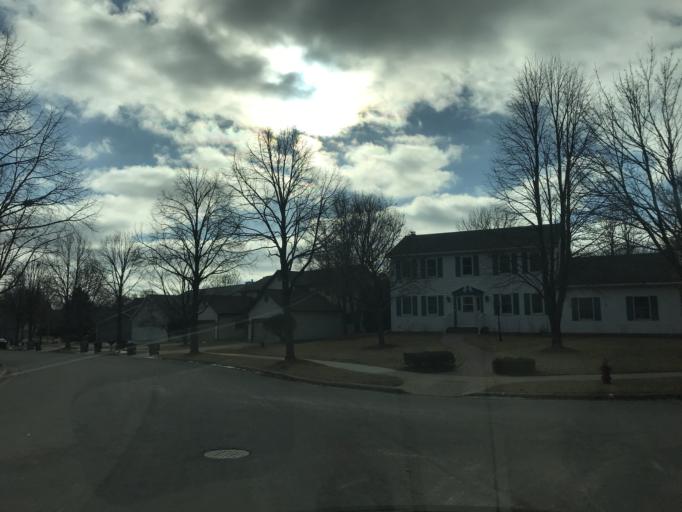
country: US
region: Wisconsin
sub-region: Dane County
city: Monona
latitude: 43.1155
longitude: -89.2981
